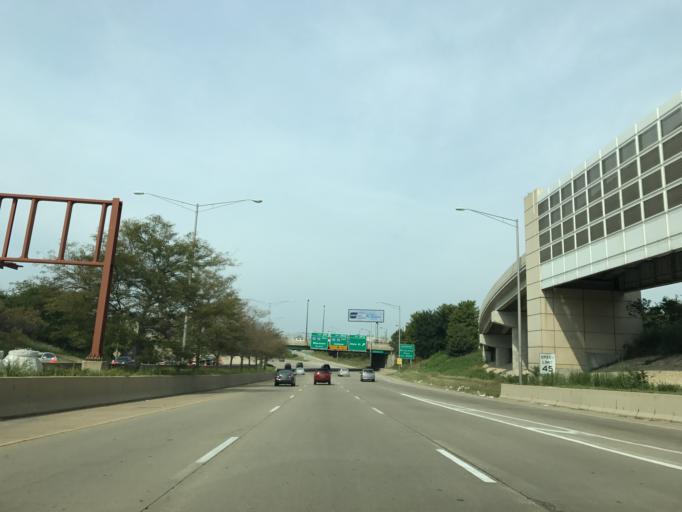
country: US
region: Illinois
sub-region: Cook County
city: Chicago
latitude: 41.8482
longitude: -87.6216
